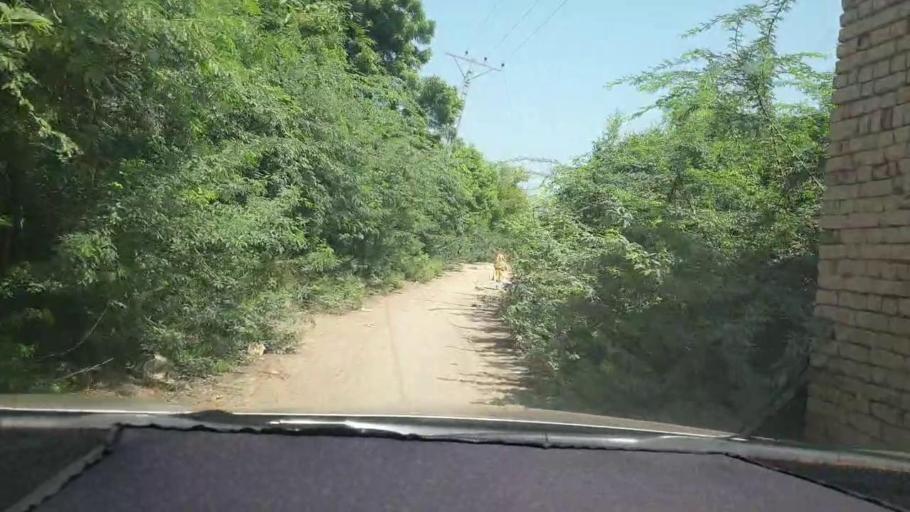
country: PK
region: Sindh
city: Kambar
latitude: 27.5918
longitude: 68.0623
